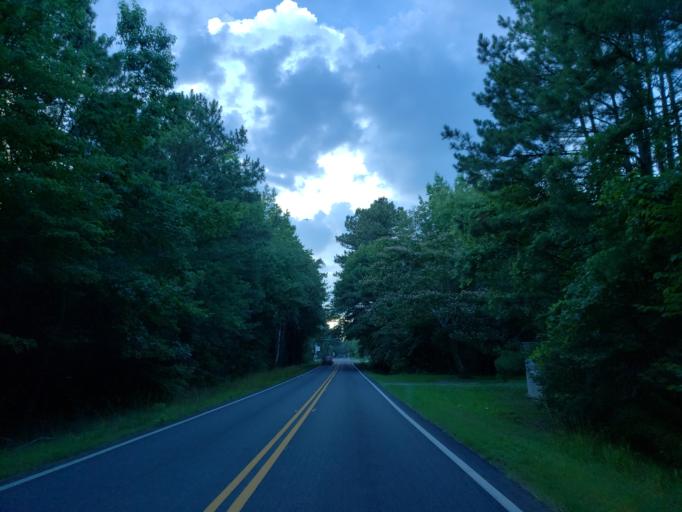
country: US
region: Georgia
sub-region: Bartow County
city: Cartersville
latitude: 34.1991
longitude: -84.7391
